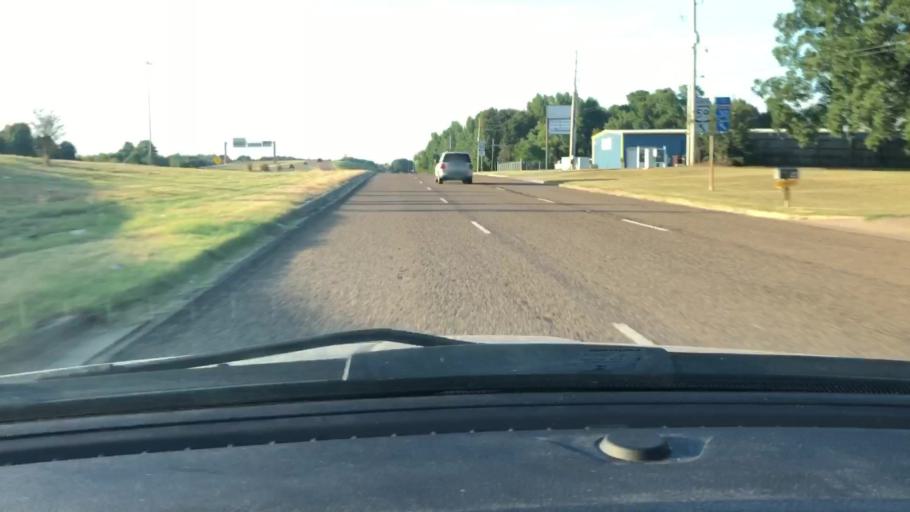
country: US
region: Texas
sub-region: Bowie County
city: Wake Village
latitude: 33.3971
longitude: -94.0973
